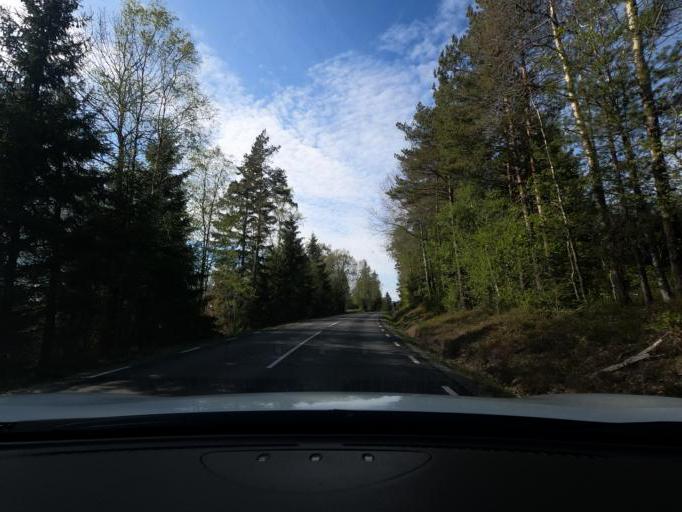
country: SE
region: Vaestra Goetaland
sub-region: Harryda Kommun
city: Landvetter
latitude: 57.6570
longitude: 12.2565
